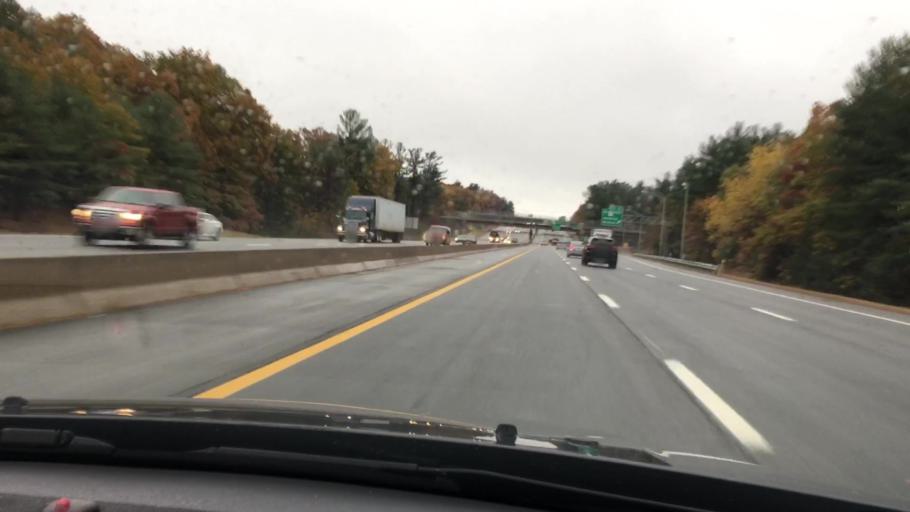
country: US
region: New Hampshire
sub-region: Hillsborough County
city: Nashua
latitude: 42.7940
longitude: -71.4967
